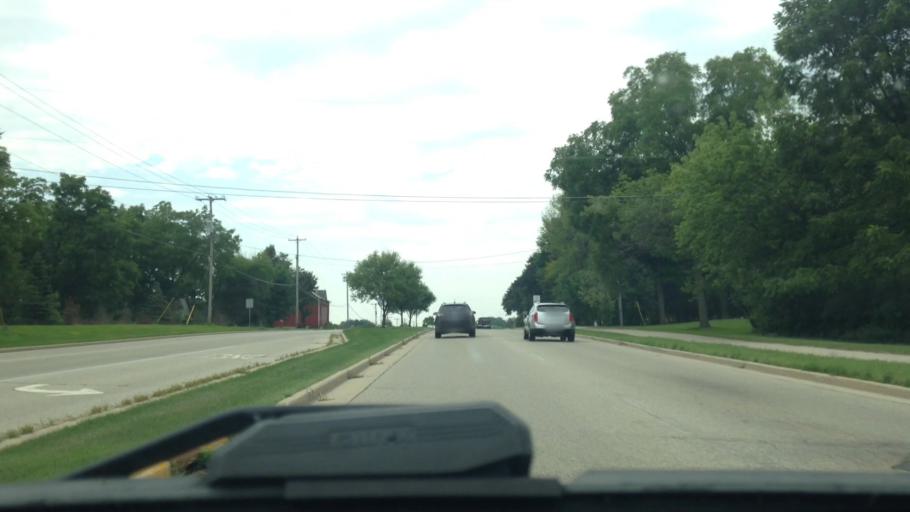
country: US
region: Wisconsin
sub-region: Waukesha County
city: Menomonee Falls
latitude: 43.1414
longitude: -88.1046
